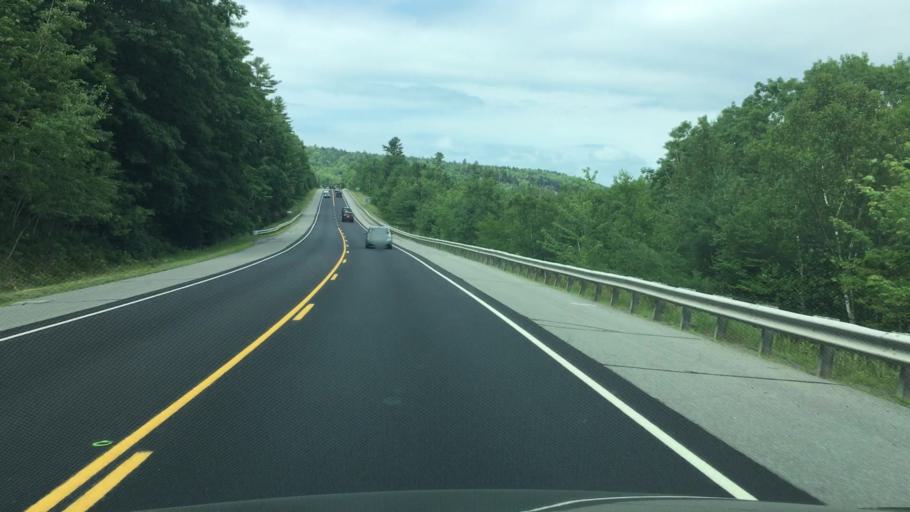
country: US
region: Maine
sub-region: Hancock County
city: Bucksport
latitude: 44.5466
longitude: -68.8091
